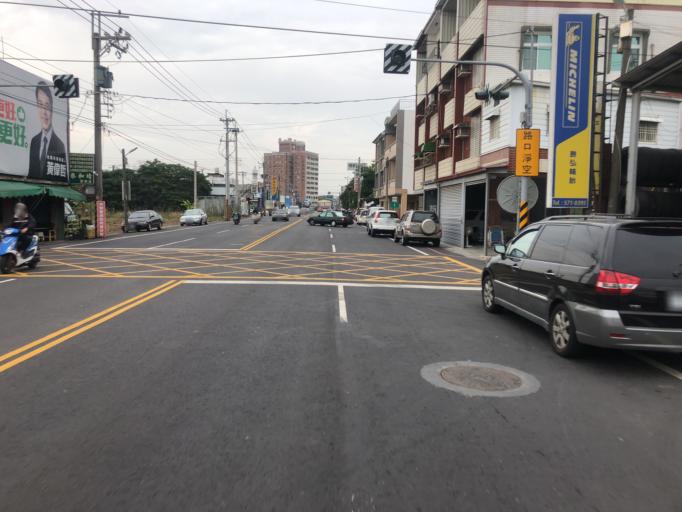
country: TW
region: Taiwan
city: Xinying
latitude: 23.1743
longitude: 120.2466
